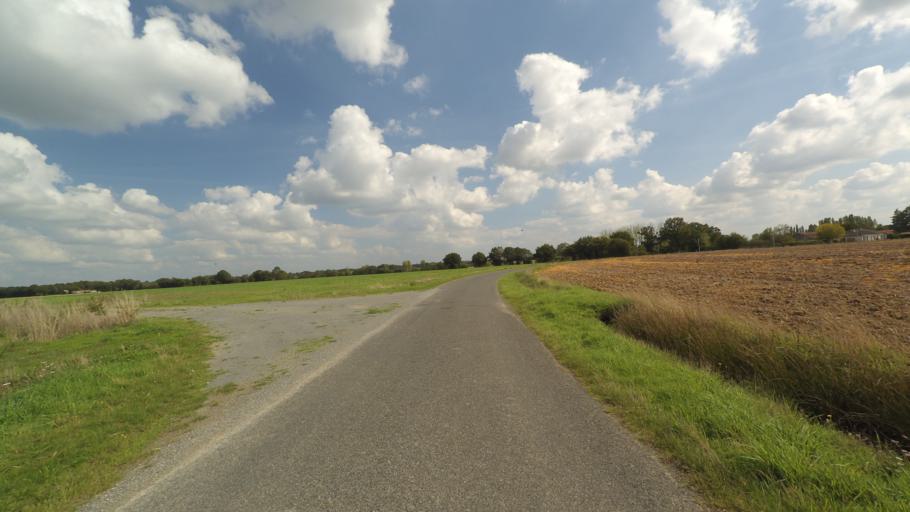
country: FR
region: Pays de la Loire
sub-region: Departement de la Vendee
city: Bouffere
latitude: 46.9661
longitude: -1.3755
